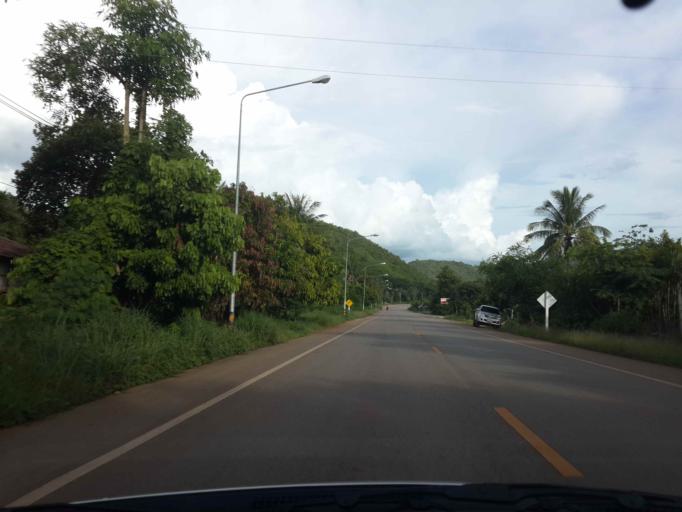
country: TH
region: Kanchanaburi
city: Sai Yok
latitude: 13.8872
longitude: 99.1655
